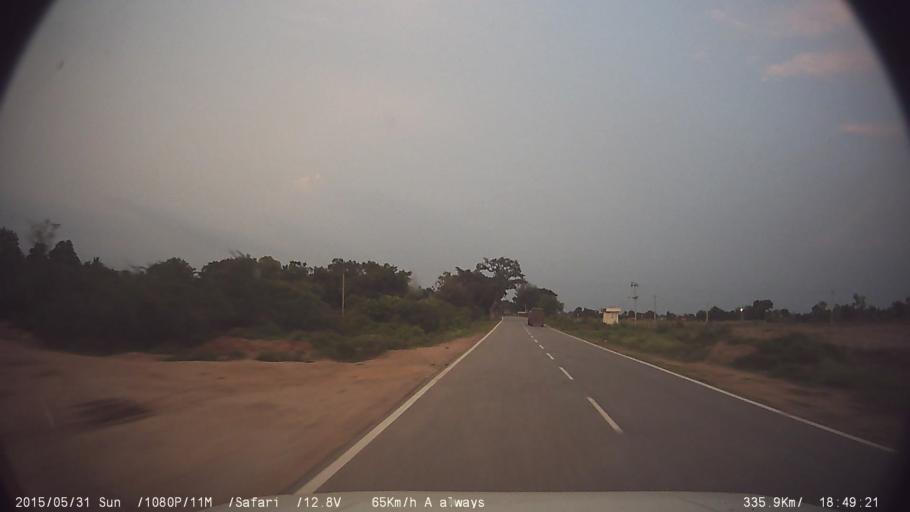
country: IN
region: Karnataka
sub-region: Mysore
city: Tirumakudal Narsipur
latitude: 12.1731
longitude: 76.8500
